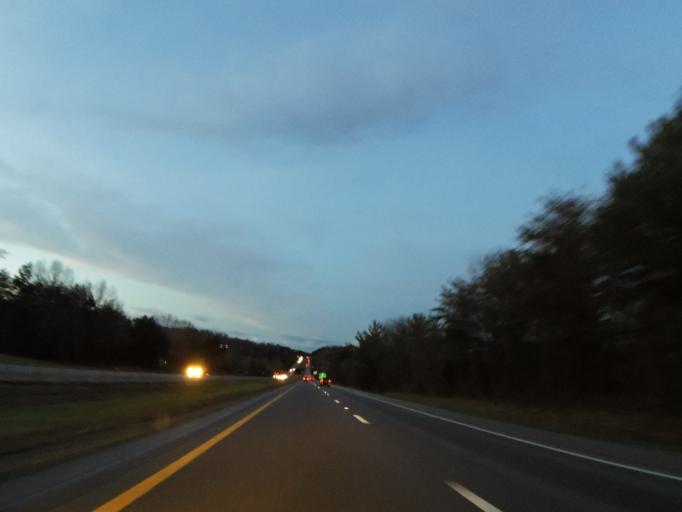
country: US
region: Kentucky
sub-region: Whitley County
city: Williamsburg
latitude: 36.7724
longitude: -84.1701
